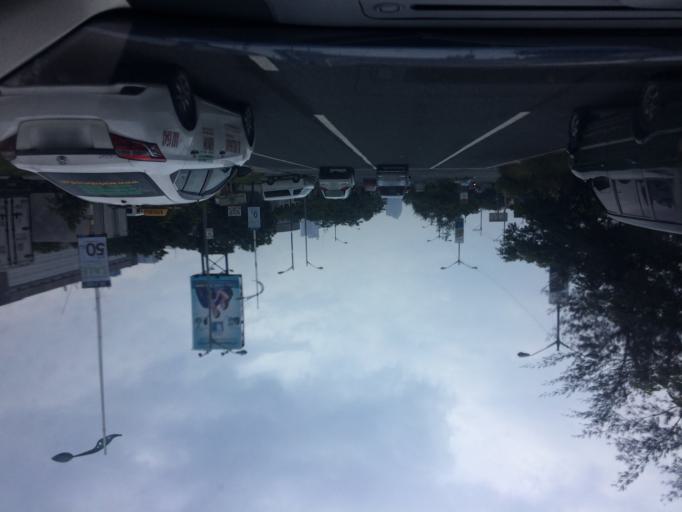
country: PH
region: Metro Manila
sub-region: City of Manila
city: Port Area
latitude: 14.5459
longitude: 120.9874
